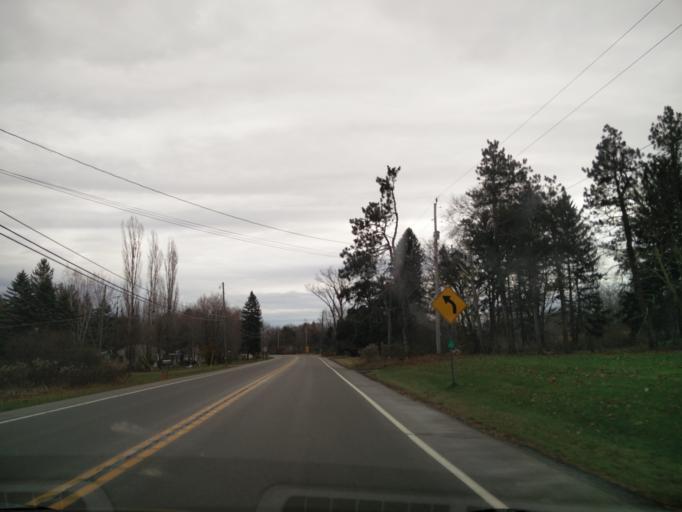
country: US
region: New York
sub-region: Tompkins County
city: Northwest Ithaca
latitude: 42.4745
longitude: -76.5535
